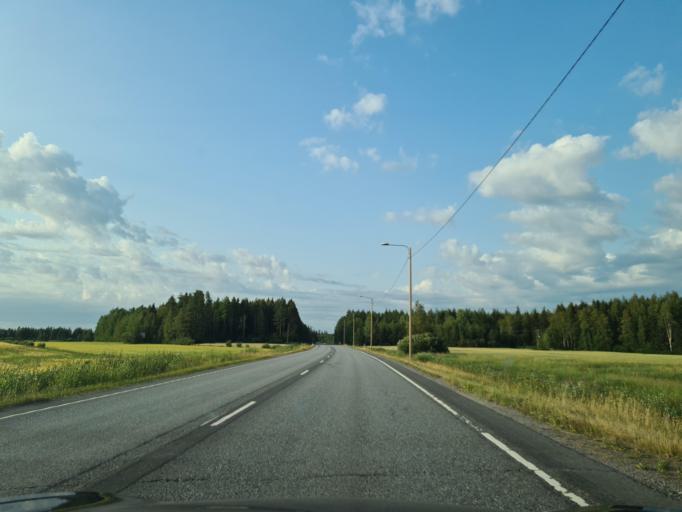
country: FI
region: Southern Ostrobothnia
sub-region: Seinaejoki
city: Kauhava
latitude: 63.0625
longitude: 23.0419
